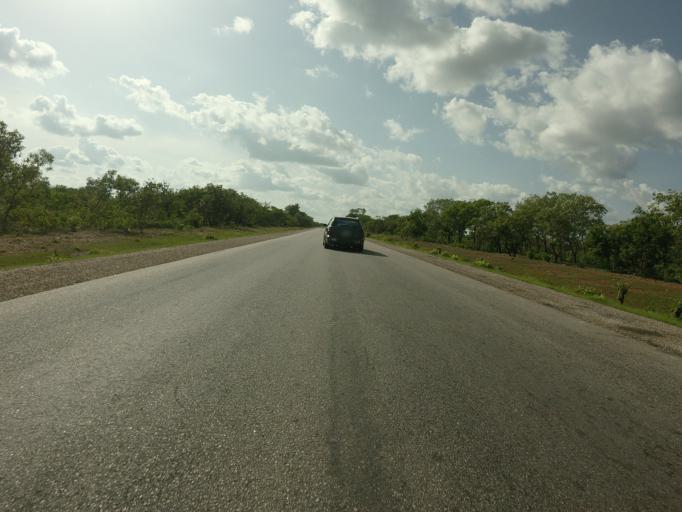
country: GH
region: Upper East
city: Bolgatanga
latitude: 10.5270
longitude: -0.8161
